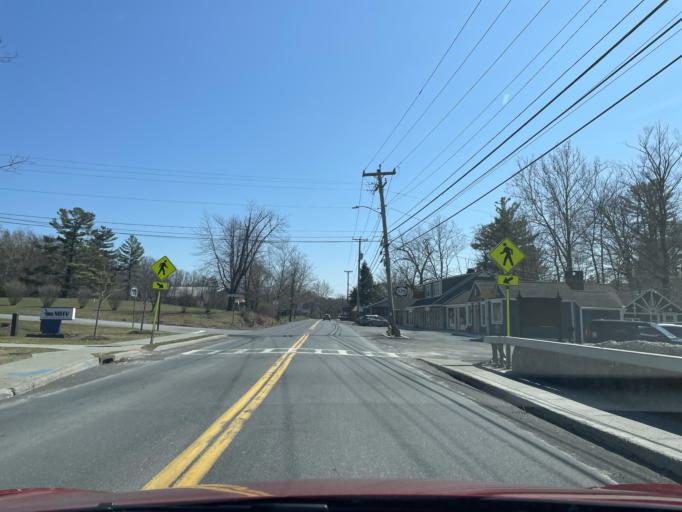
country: US
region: New York
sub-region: Ulster County
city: Woodstock
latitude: 42.0381
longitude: -74.1127
